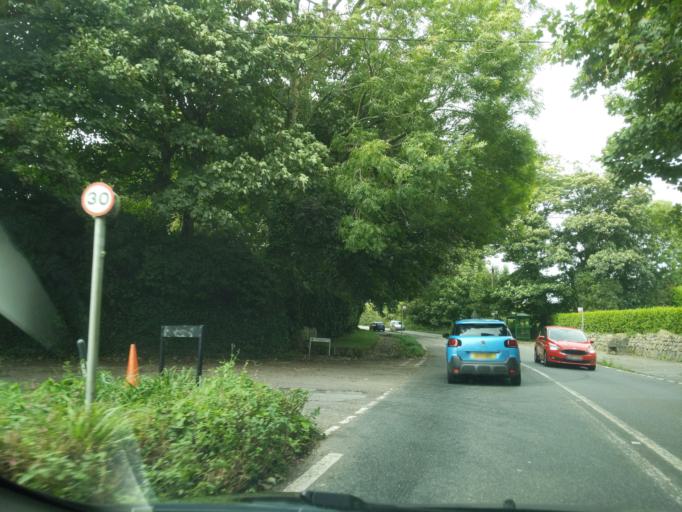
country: GB
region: England
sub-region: Cornwall
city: Porthleven
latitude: 50.1069
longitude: -5.3336
